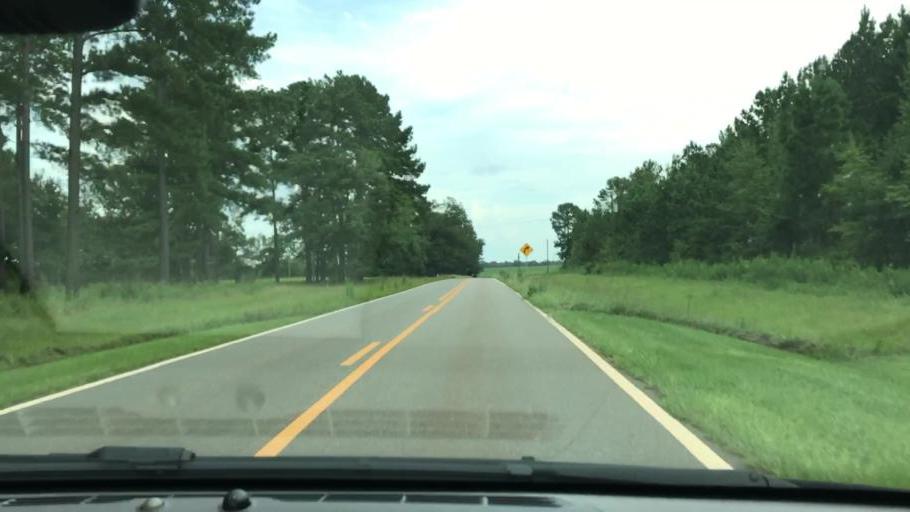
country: US
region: Georgia
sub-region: Early County
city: Blakely
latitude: 31.4542
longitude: -84.9147
